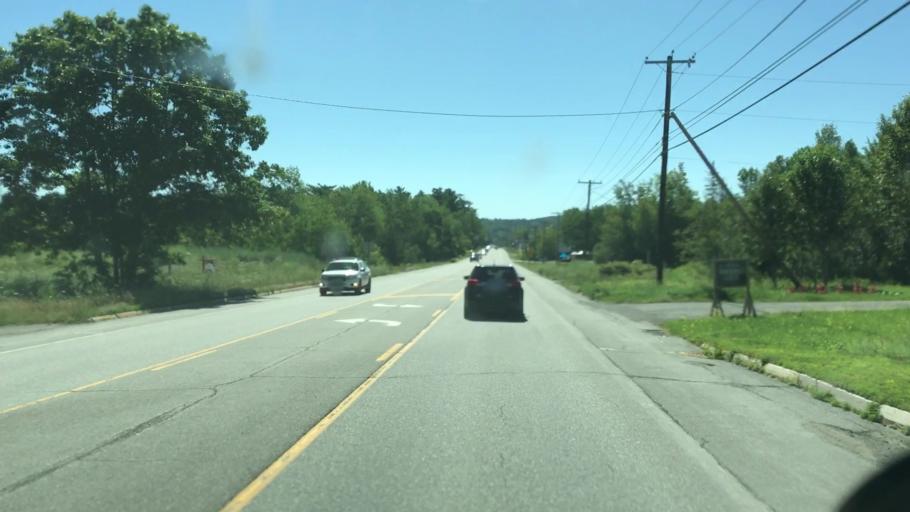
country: US
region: Maine
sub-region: Penobscot County
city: Holden
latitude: 44.7624
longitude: -68.7006
